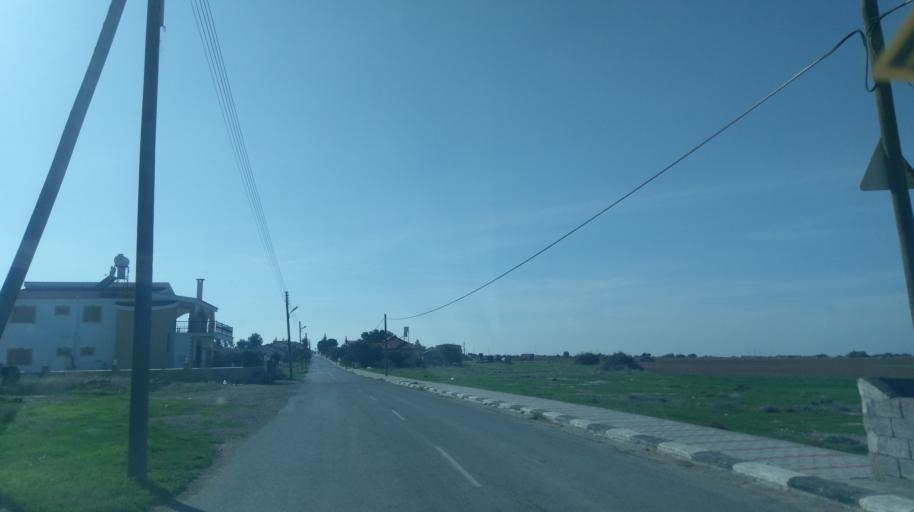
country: CY
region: Larnaka
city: Athienou
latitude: 35.1732
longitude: 33.5449
